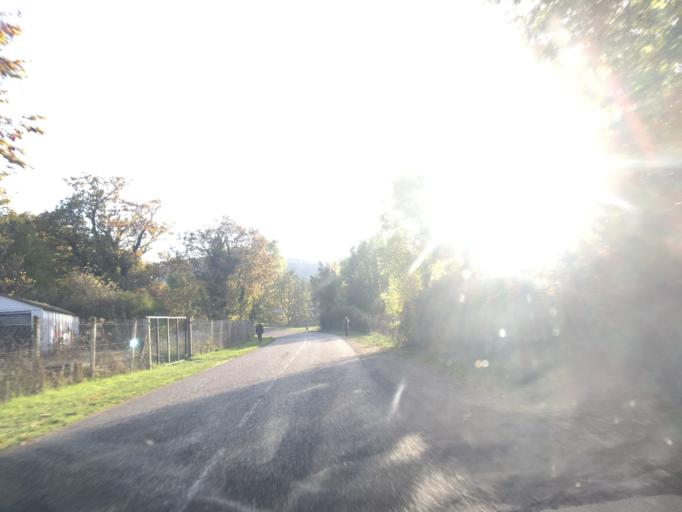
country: FR
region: Haute-Normandie
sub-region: Departement de l'Eure
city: Heudreville-sur-Eure
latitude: 49.1047
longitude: 1.2413
